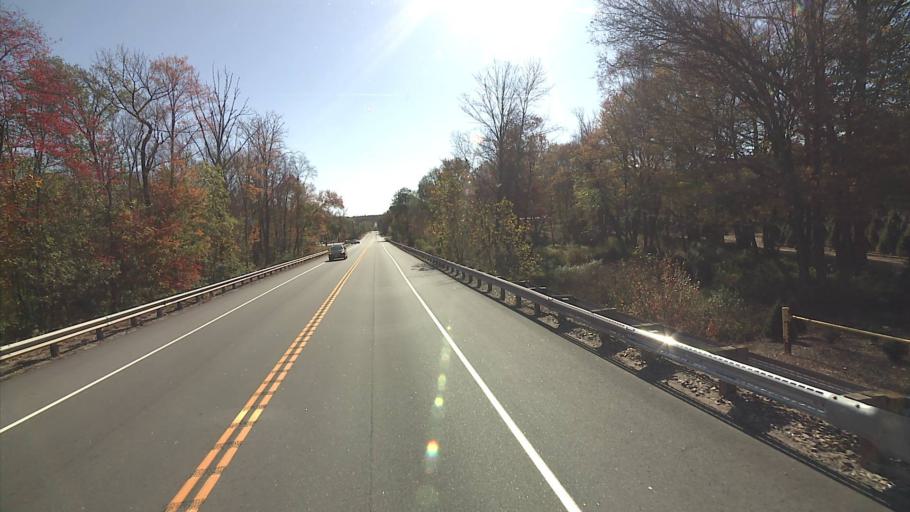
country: US
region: Connecticut
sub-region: Tolland County
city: Coventry Lake
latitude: 41.7338
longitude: -72.3588
